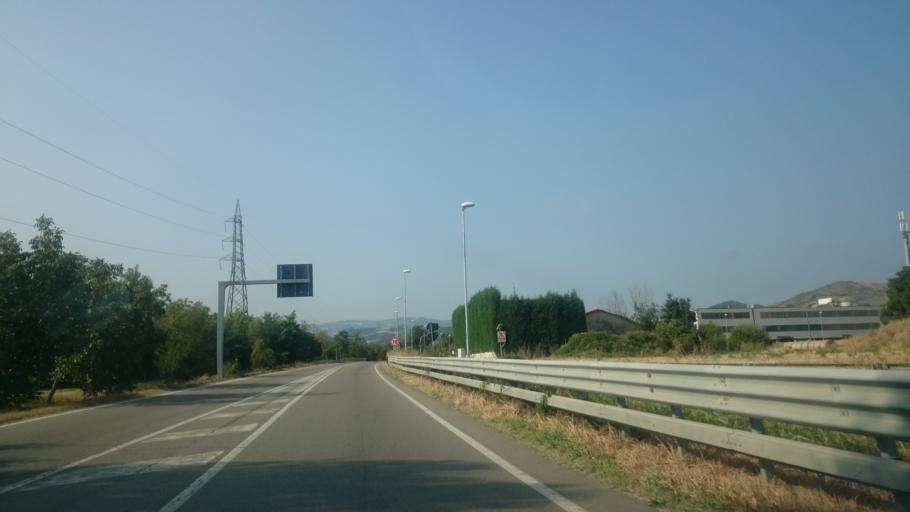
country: IT
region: Emilia-Romagna
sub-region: Provincia di Reggio Emilia
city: Castellarano
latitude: 44.5164
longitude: 10.7432
